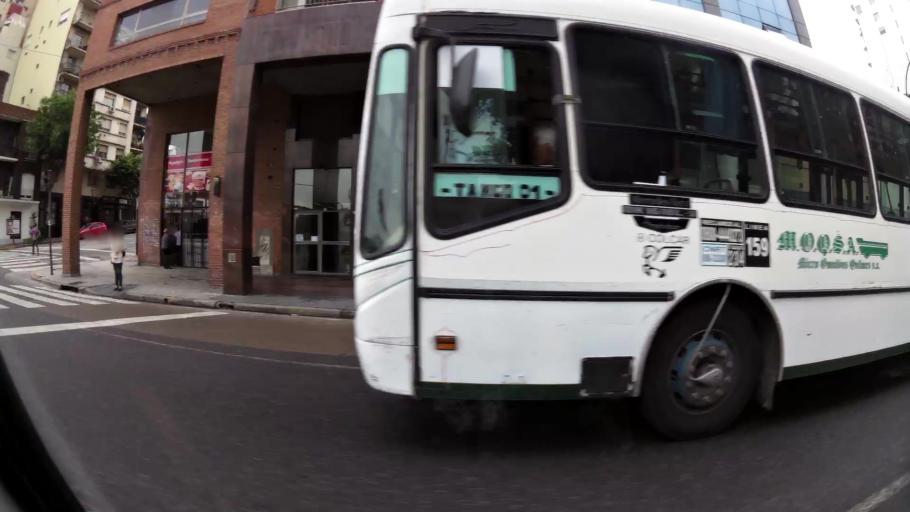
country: AR
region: Buenos Aires F.D.
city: Buenos Aires
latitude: -34.6213
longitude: -58.3684
